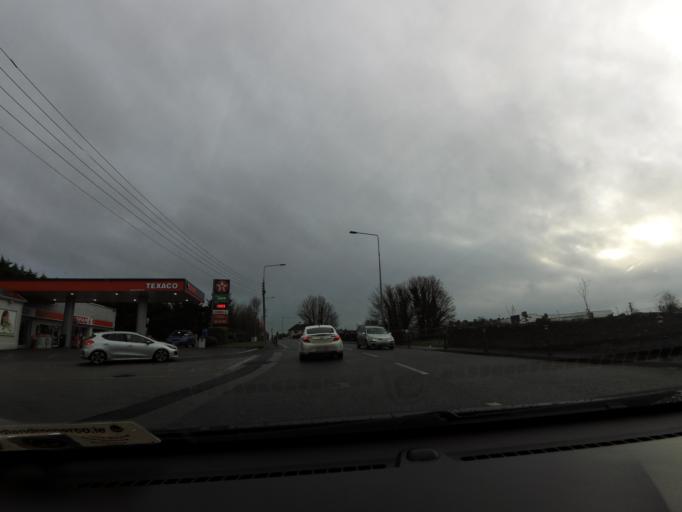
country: IE
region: Munster
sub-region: North Tipperary
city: Roscrea
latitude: 52.9582
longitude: -7.8018
